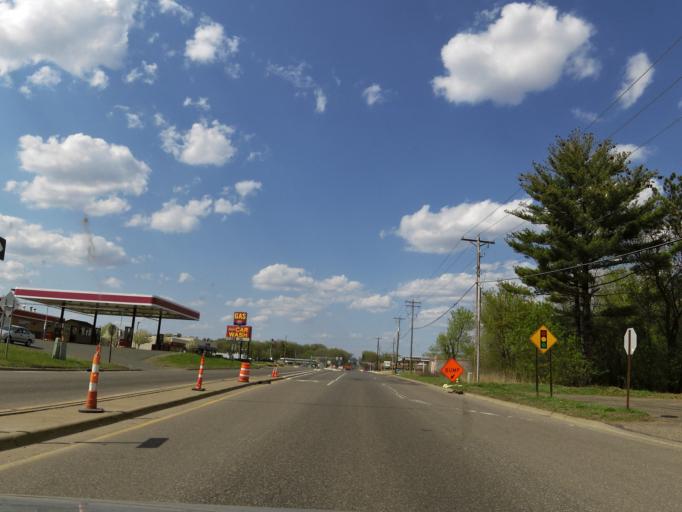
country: US
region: Minnesota
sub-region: Washington County
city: Oak Park Heights
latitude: 45.0334
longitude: -92.8074
